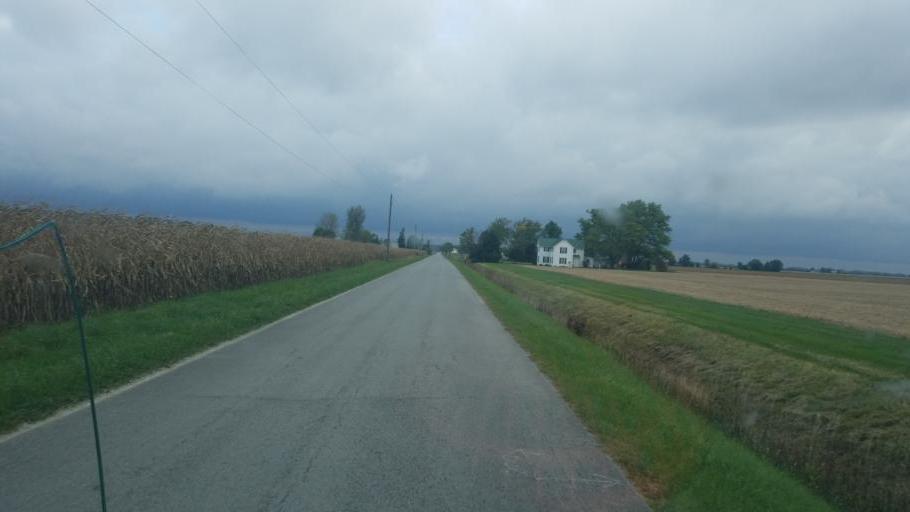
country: US
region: Ohio
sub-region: Wood County
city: North Baltimore
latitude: 41.1580
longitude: -83.5928
